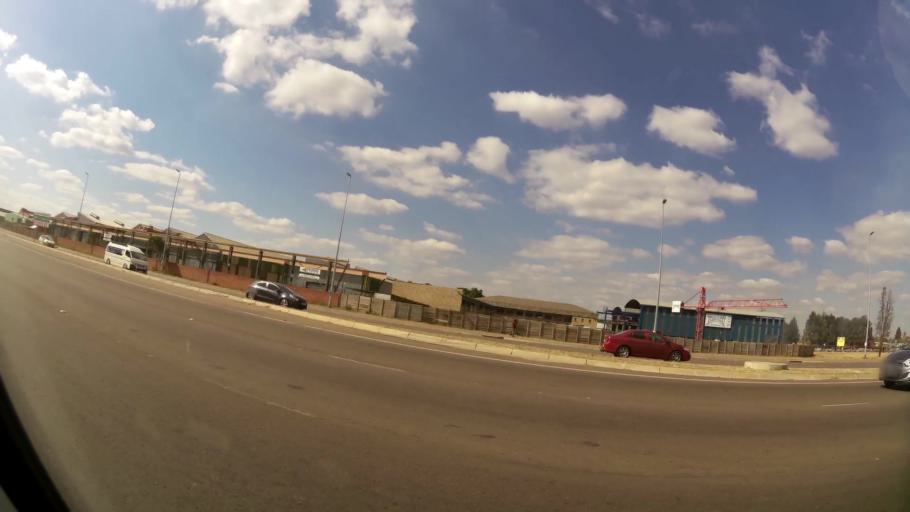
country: ZA
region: Gauteng
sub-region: City of Tshwane Metropolitan Municipality
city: Pretoria
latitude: -25.7373
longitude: 28.3296
